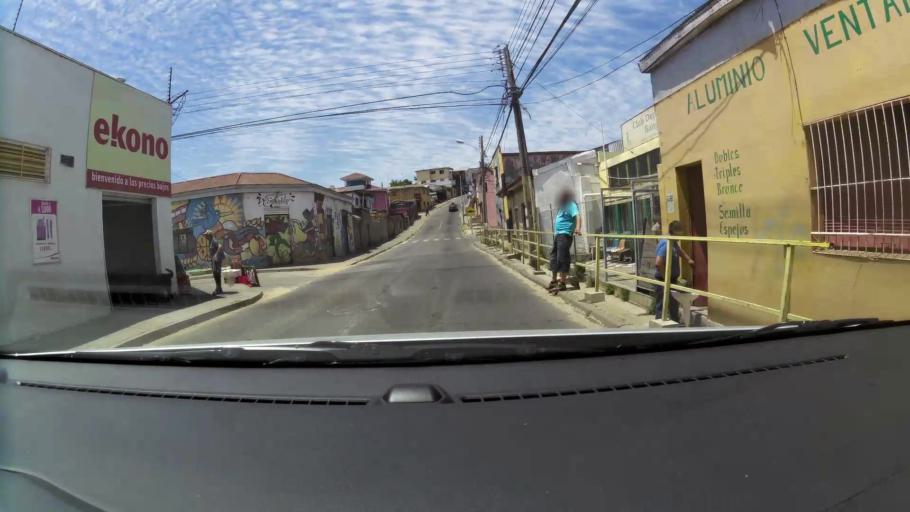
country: CL
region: Valparaiso
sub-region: Provincia de Valparaiso
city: Valparaiso
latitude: -33.0471
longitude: -71.5945
